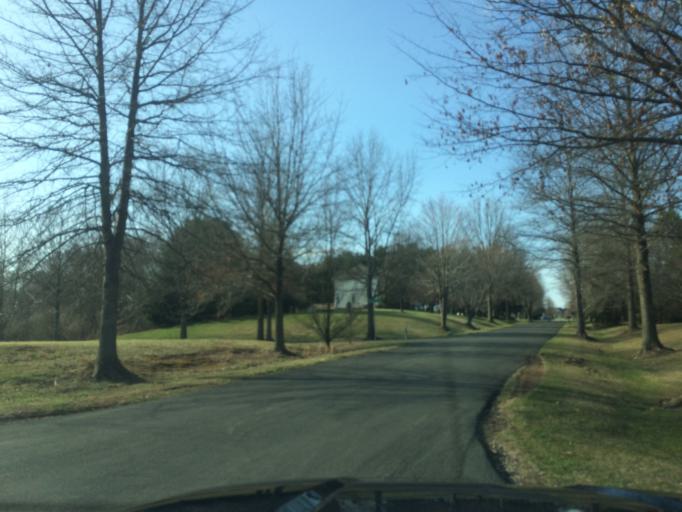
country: US
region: Maryland
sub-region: Carroll County
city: Sykesville
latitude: 39.2805
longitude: -76.9707
